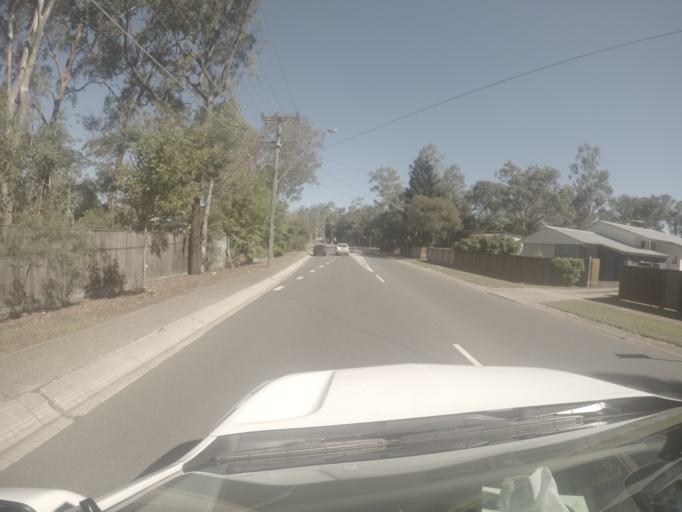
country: AU
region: Queensland
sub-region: Ipswich
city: Springfield
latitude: -27.6316
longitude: 152.9158
